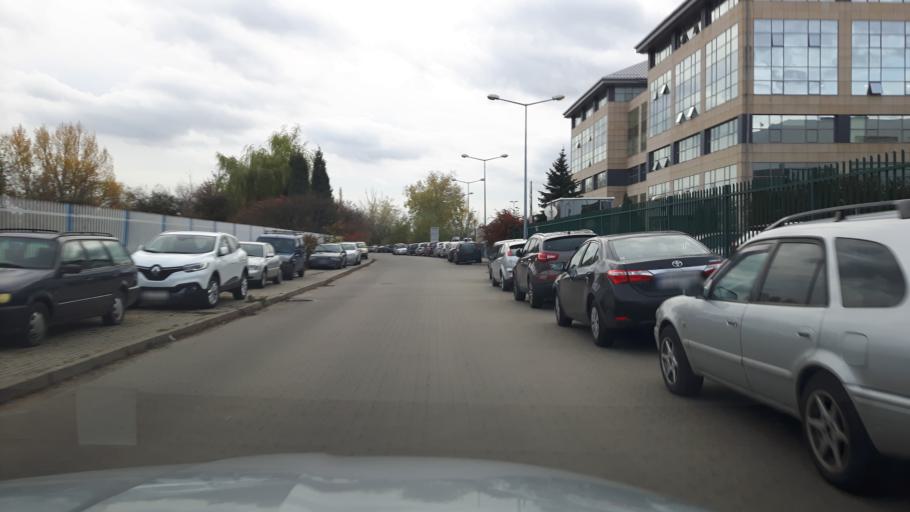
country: PL
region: Masovian Voivodeship
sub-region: Warszawa
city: Wlochy
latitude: 52.1725
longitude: 20.9891
